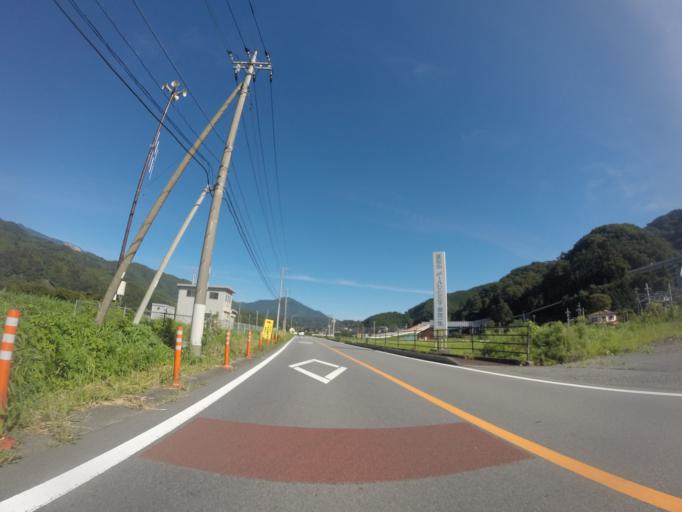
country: JP
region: Shizuoka
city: Fujinomiya
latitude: 35.3295
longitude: 138.4516
